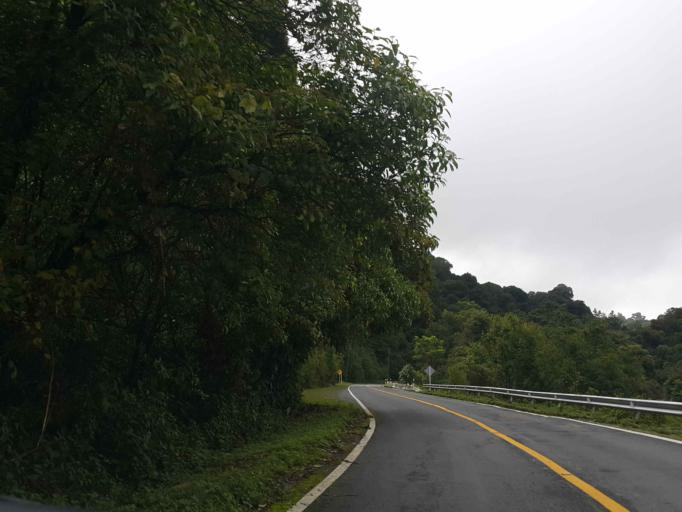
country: TH
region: Chiang Mai
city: Mae Chaem
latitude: 18.5651
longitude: 98.4850
